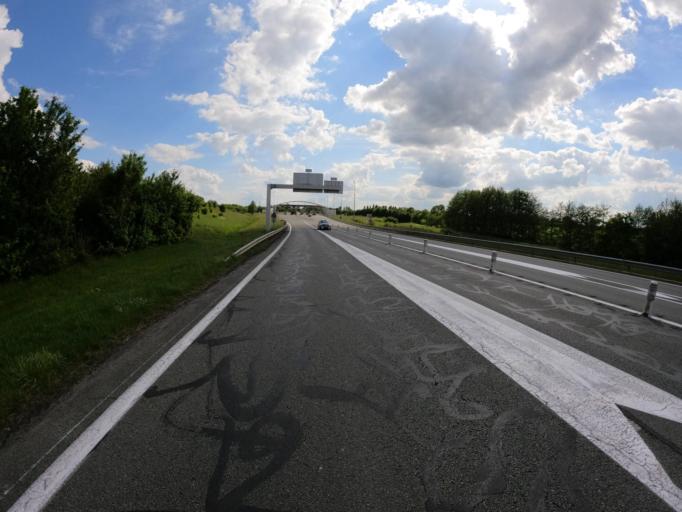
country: FR
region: Pays de la Loire
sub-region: Departement de Maine-et-Loire
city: Nuaille
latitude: 47.0853
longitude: -0.8268
